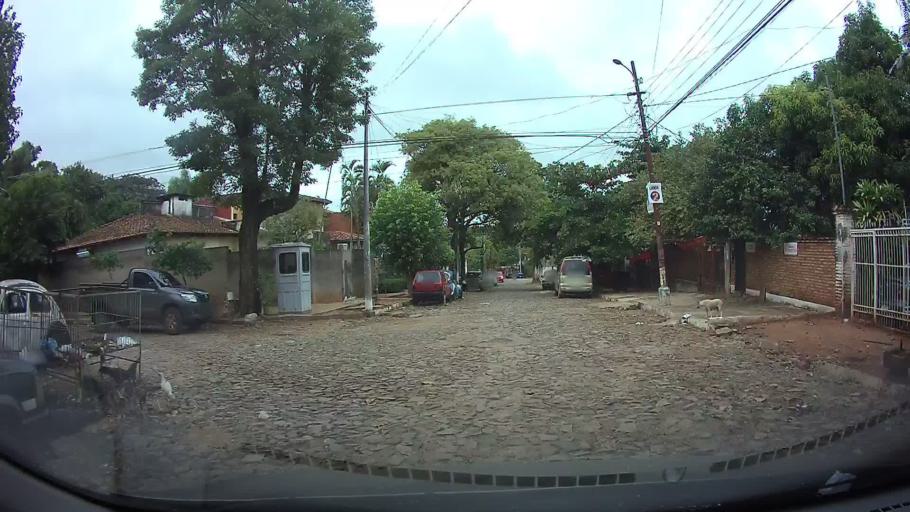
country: PY
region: Asuncion
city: Asuncion
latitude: -25.3196
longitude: -57.6162
